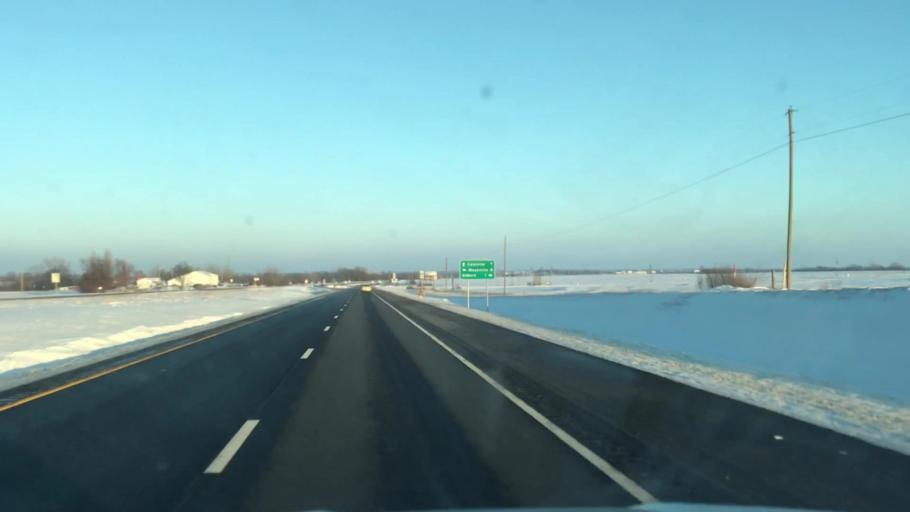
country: US
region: Missouri
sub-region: Clinton County
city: Cameron
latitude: 39.7615
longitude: -94.3624
